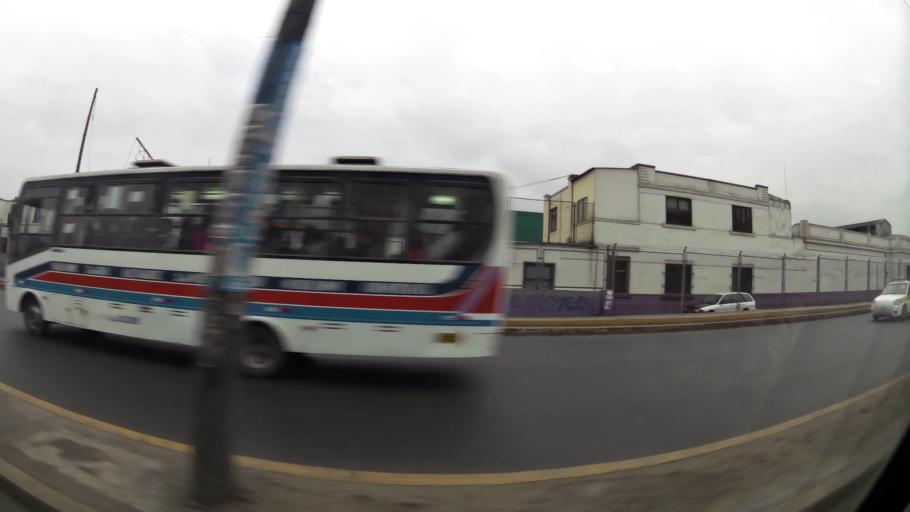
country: PE
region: Lima
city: Lima
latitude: -12.0477
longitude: -77.0557
